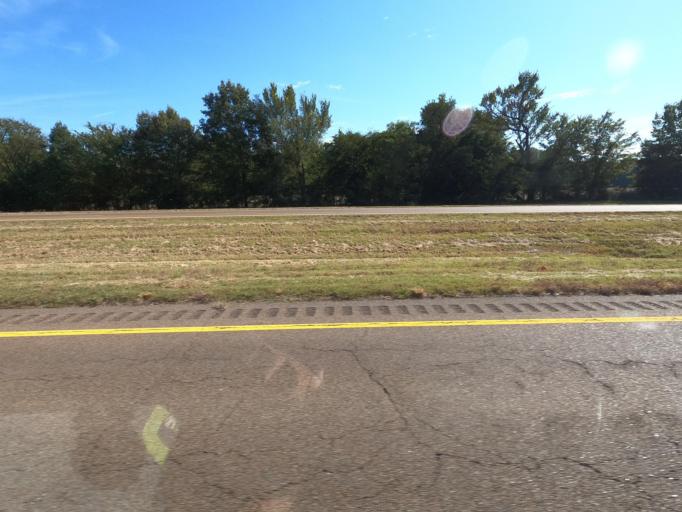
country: US
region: Tennessee
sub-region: Obion County
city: South Fulton
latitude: 36.4815
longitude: -88.9433
